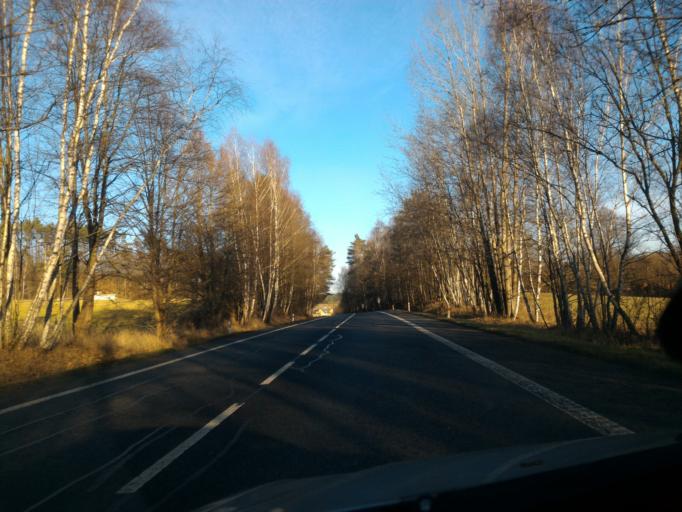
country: CZ
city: Jablonne v Podjestedi
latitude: 50.7792
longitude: 14.7804
